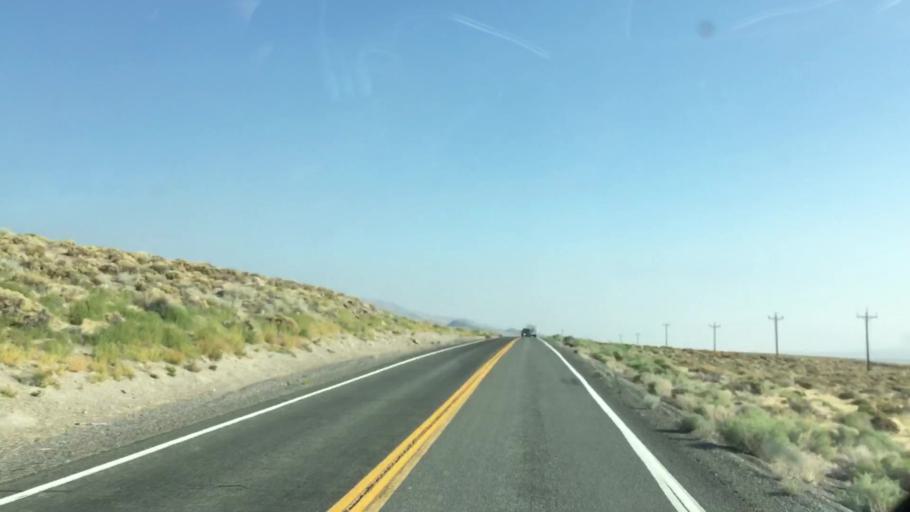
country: US
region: Nevada
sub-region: Lyon County
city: Fernley
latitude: 40.0115
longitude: -119.3878
